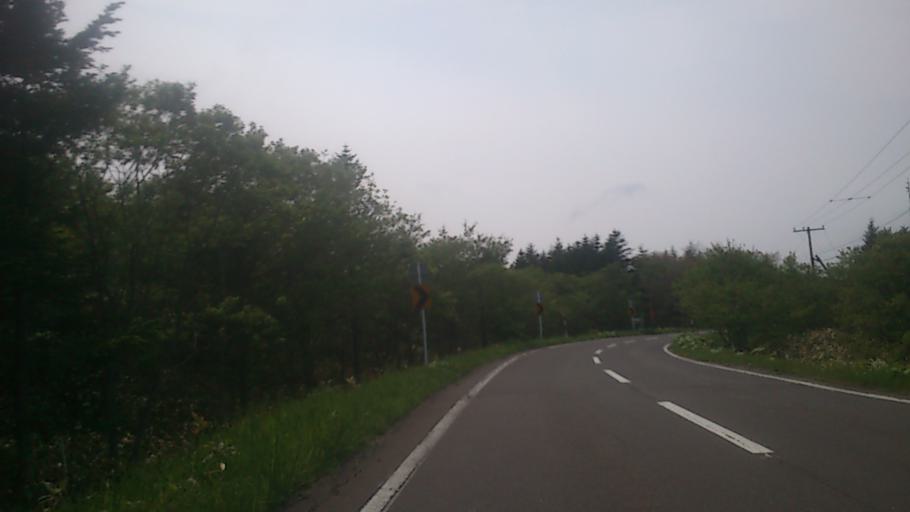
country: JP
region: Hokkaido
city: Nemuro
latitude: 43.2060
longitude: 145.3481
